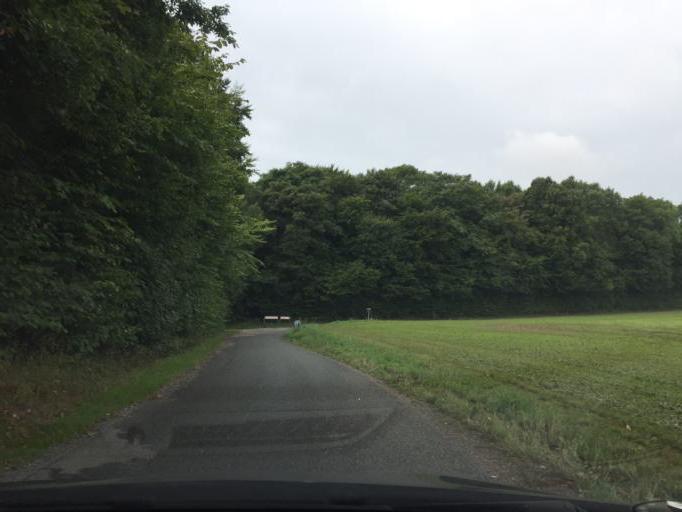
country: DK
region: South Denmark
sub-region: Assens Kommune
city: Harby
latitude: 55.1986
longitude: 10.0357
